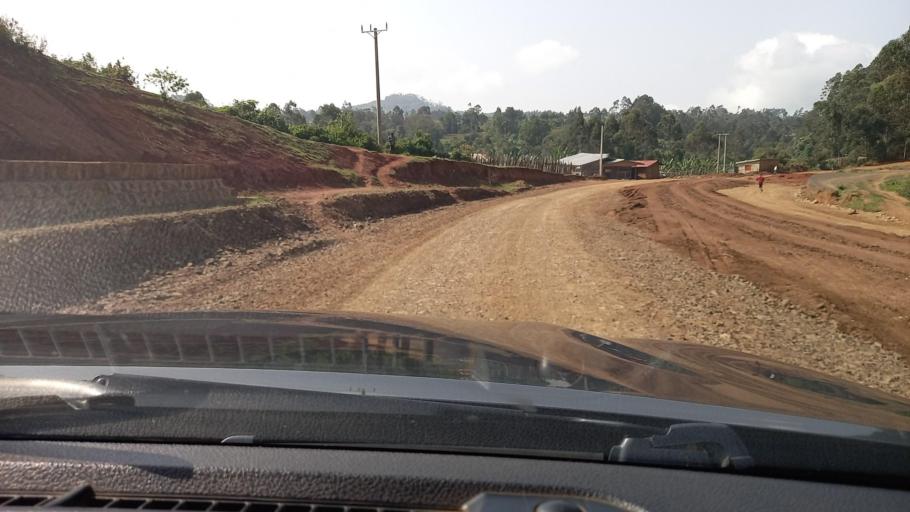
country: ET
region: Southern Nations, Nationalities, and People's Region
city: Mizan Teferi
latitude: 6.1729
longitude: 35.5864
